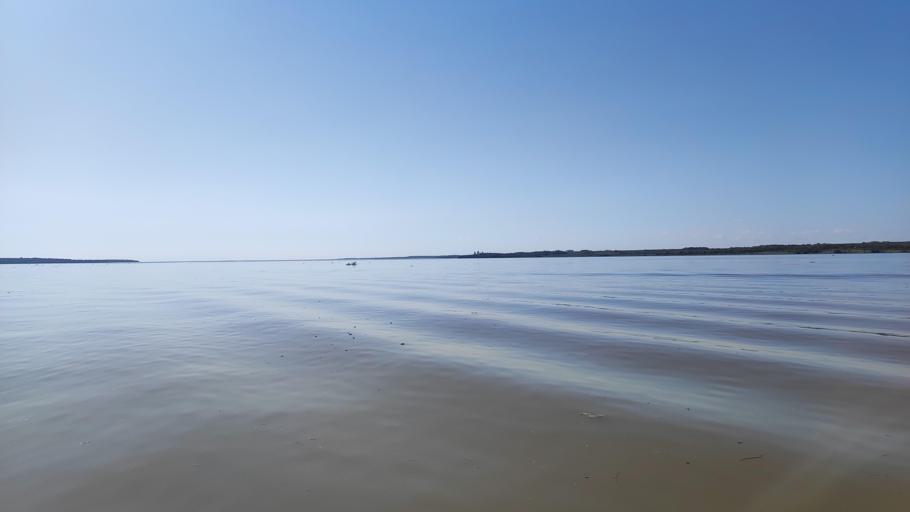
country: PY
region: Itapua
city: San Juan del Parana
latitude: -27.3383
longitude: -55.9944
